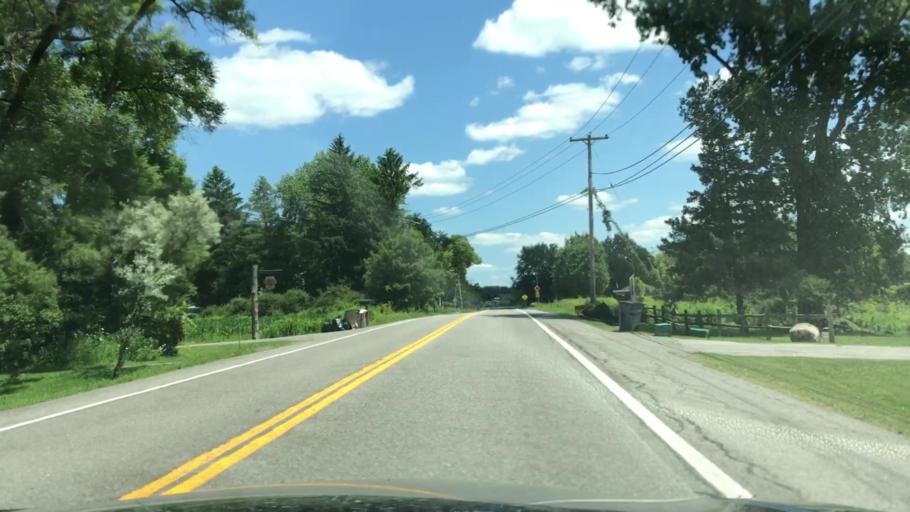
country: US
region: New York
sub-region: Erie County
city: East Aurora
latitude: 42.7686
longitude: -78.5435
